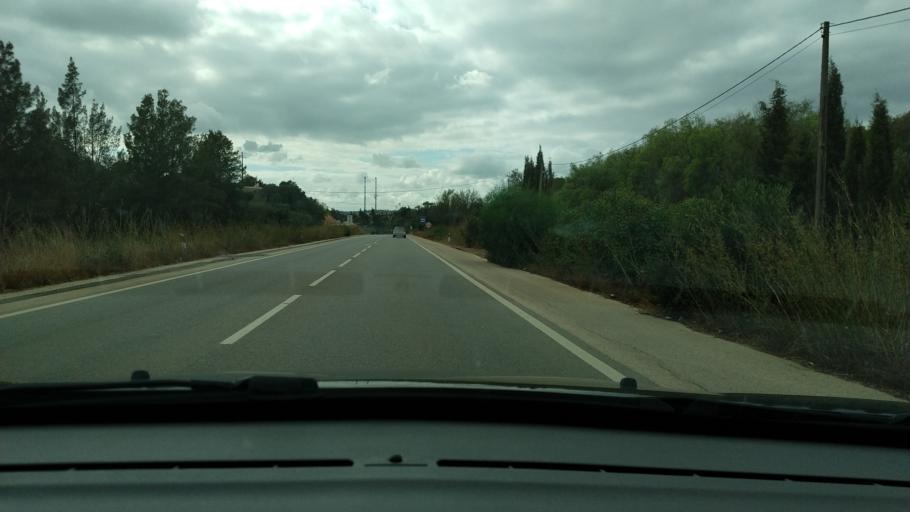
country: PT
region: Faro
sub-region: Lagos
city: Lagos
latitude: 37.0995
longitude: -8.7527
